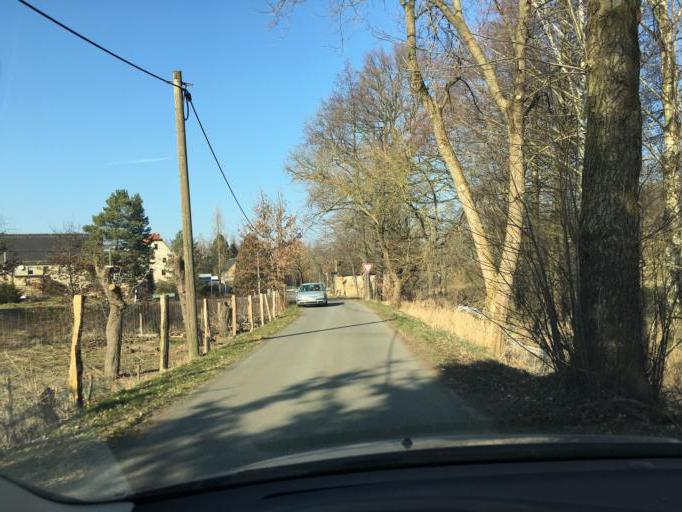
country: DE
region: Thuringia
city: Frohnsdorf
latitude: 50.9074
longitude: 12.5718
